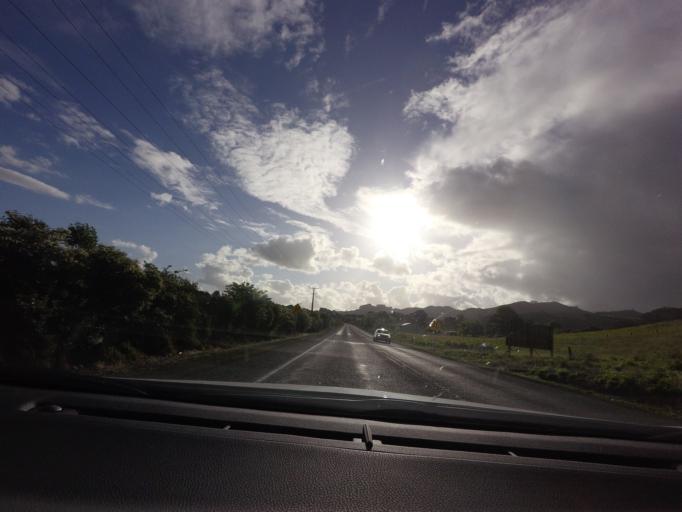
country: NZ
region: Auckland
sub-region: Auckland
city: Pukekohe East
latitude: -37.2171
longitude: 175.0511
